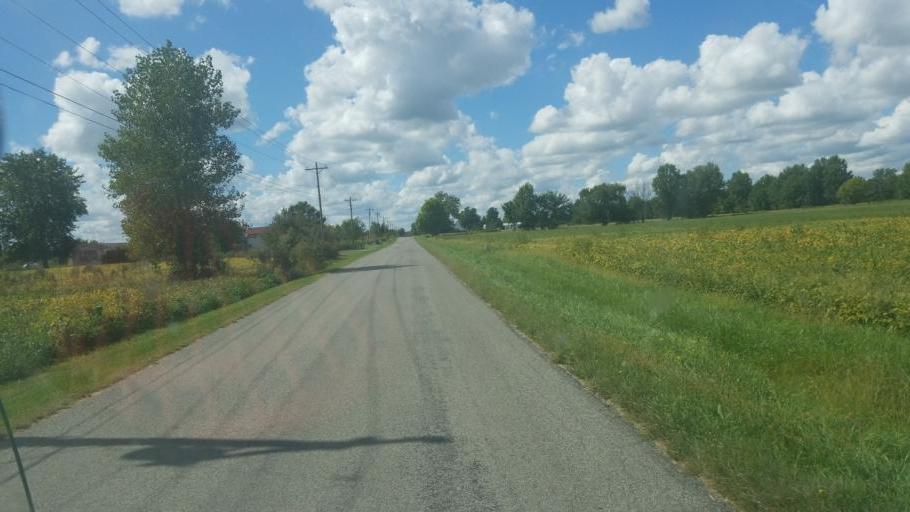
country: US
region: Ohio
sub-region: Champaign County
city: North Lewisburg
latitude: 40.3296
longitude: -83.4949
